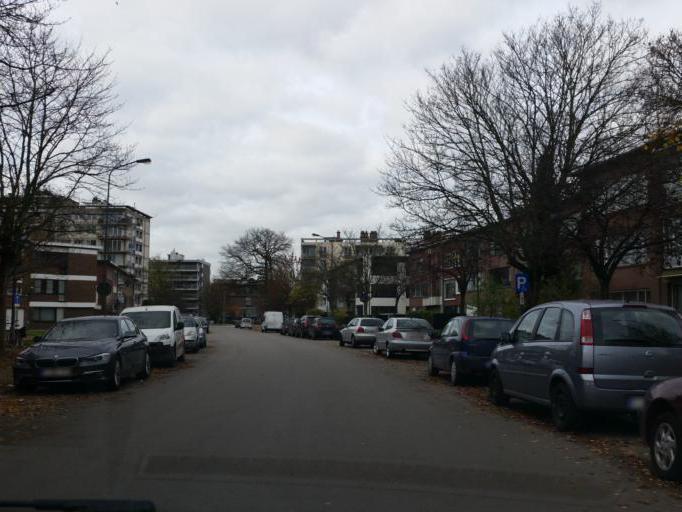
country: BE
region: Flanders
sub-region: Provincie Antwerpen
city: Mortsel
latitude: 51.1813
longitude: 4.4396
